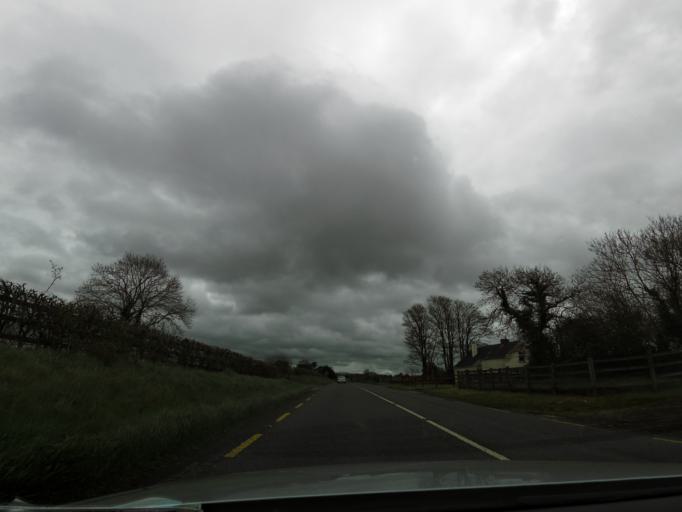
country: IE
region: Leinster
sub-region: Kilkenny
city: Ballyragget
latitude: 52.7187
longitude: -7.3415
